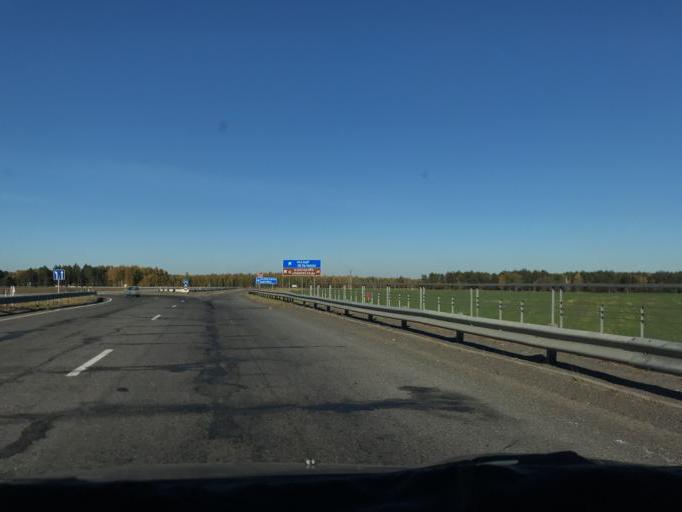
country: BY
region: Gomel
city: Mazyr
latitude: 52.0063
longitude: 29.2563
